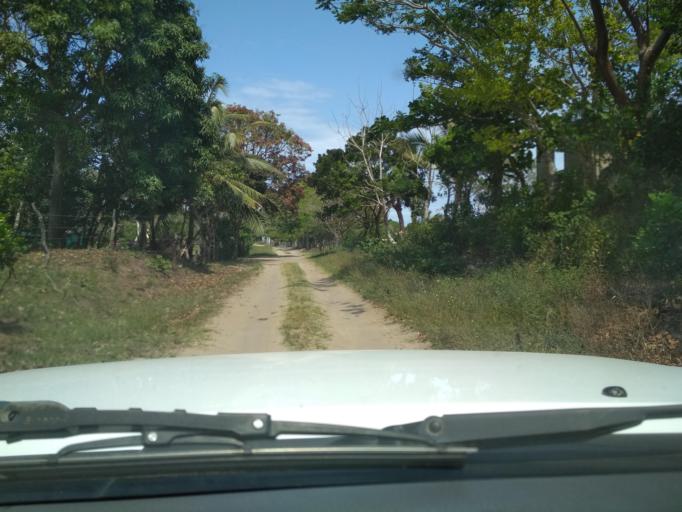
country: MX
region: Veracruz
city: Anton Lizardo
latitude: 19.0088
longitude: -95.9891
